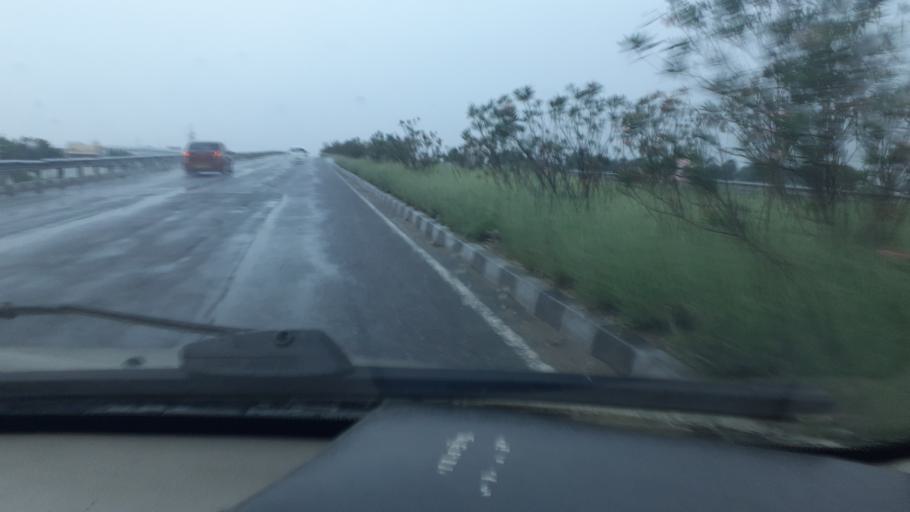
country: IN
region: Tamil Nadu
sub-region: Virudhunagar
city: Sattur
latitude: 9.3826
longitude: 77.9139
